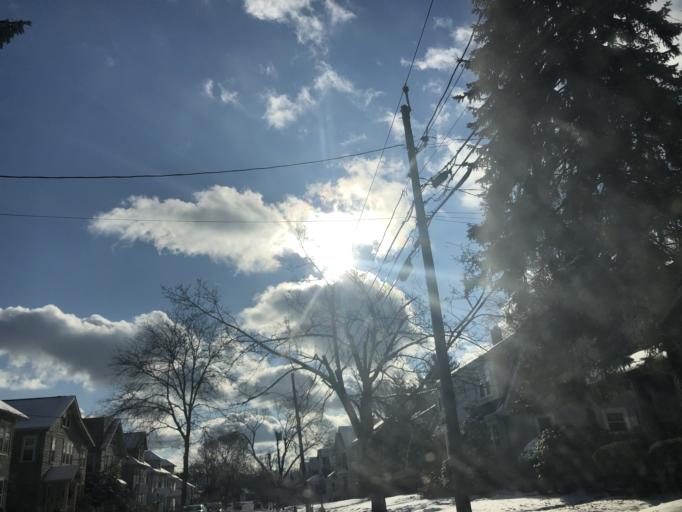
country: US
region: Massachusetts
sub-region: Middlesex County
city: Arlington
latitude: 42.4212
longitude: -71.1464
